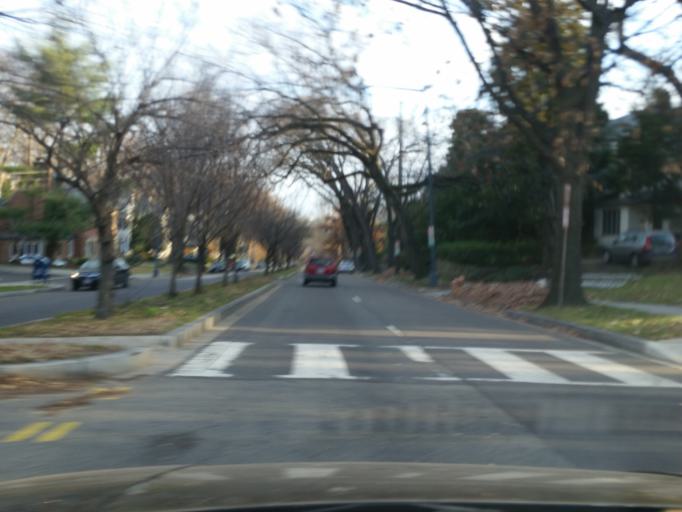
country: US
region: Washington, D.C.
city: Washington, D.C.
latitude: 38.9264
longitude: -77.0617
